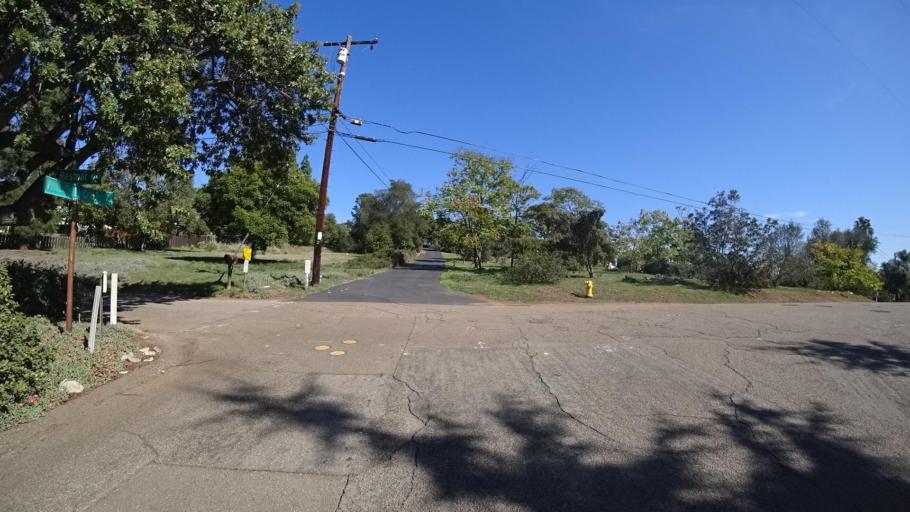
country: US
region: California
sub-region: San Diego County
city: Casa de Oro-Mount Helix
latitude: 32.7661
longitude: -116.9751
